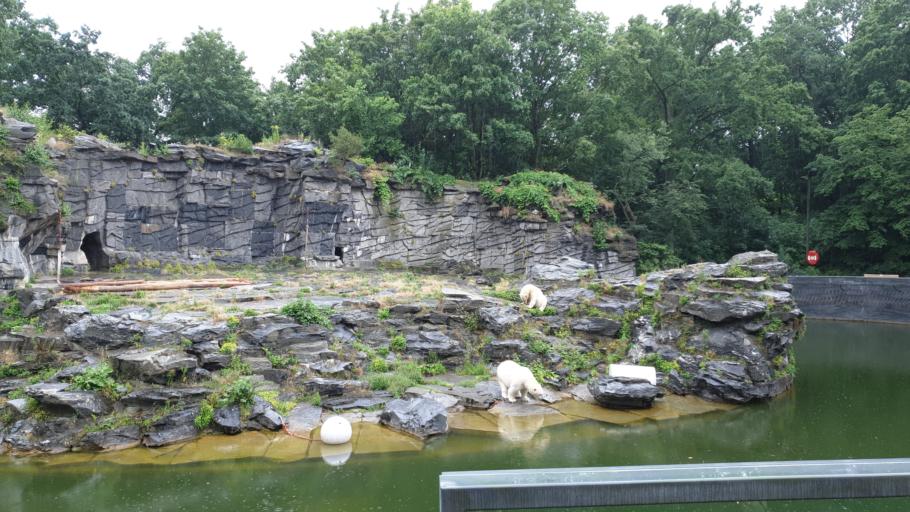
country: DE
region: Berlin
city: Karlshorst
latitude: 52.4973
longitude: 13.5276
